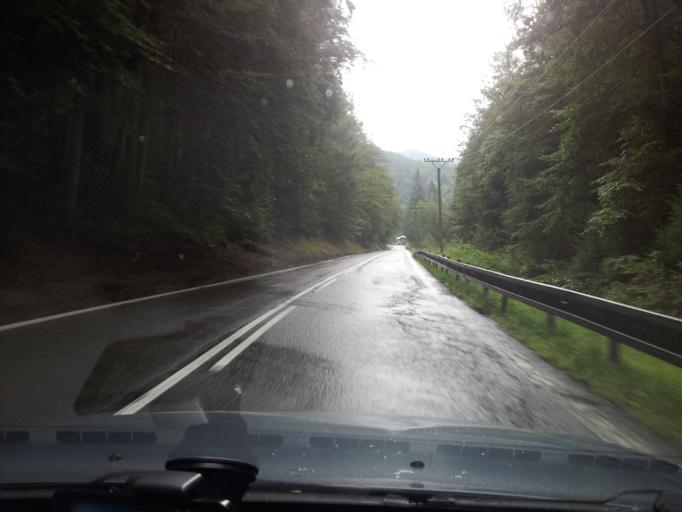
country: SK
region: Banskobystricky
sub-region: Okres Banska Bystrica
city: Brezno
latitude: 48.8897
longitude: 19.6818
